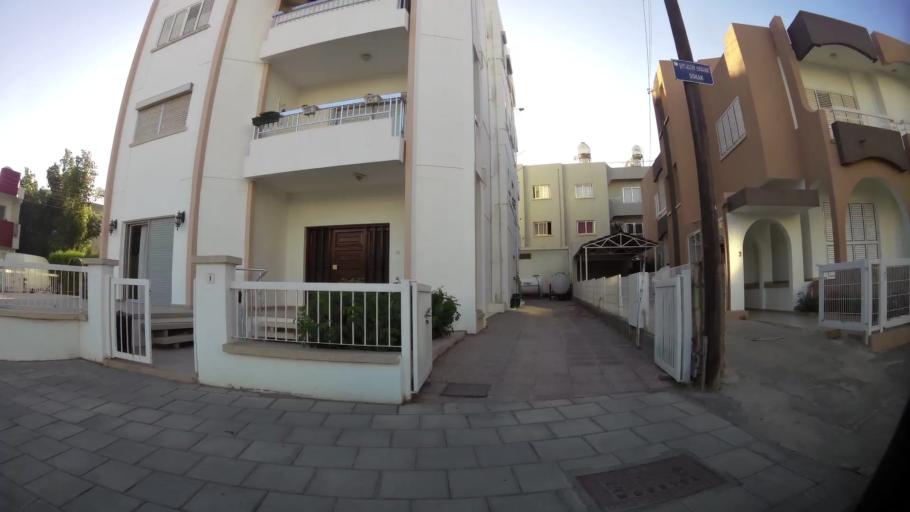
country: CY
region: Lefkosia
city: Nicosia
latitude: 35.2043
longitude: 33.3296
